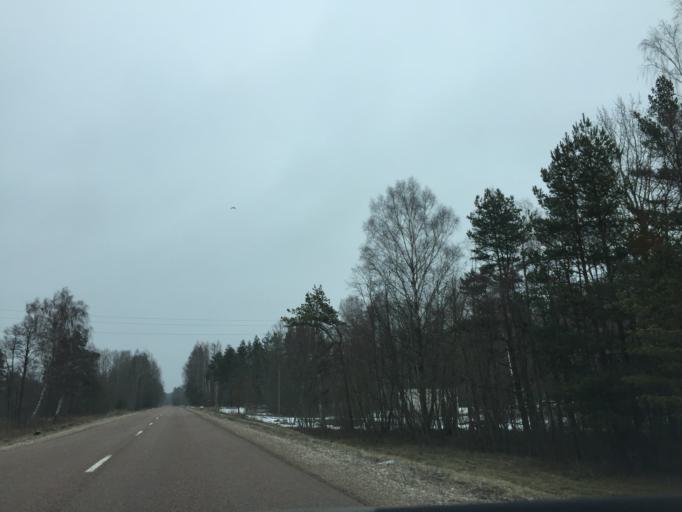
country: LV
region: Olaine
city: Olaine
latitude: 56.6301
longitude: 23.9333
